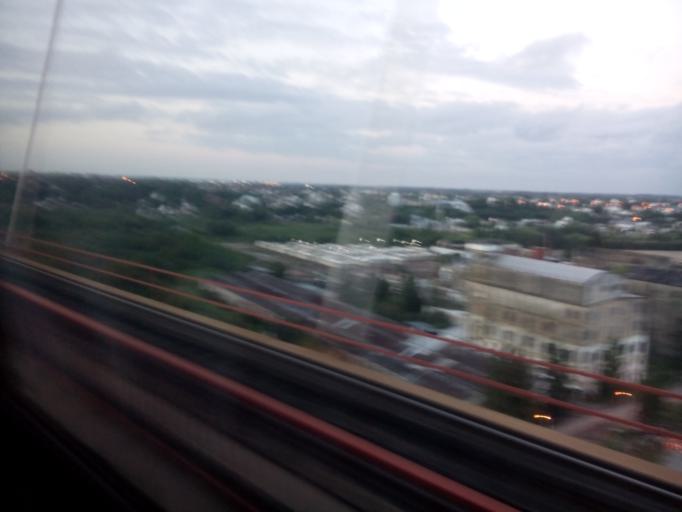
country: AR
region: Buenos Aires
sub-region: Partido de Zarate
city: Zarate
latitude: -34.1047
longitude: -59.0028
